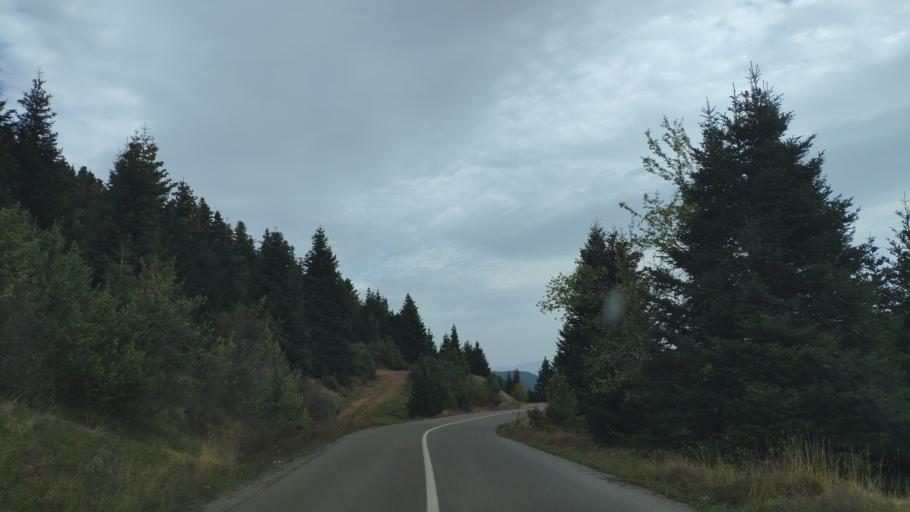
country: GR
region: Central Greece
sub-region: Nomos Fokidos
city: Amfissa
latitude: 38.7104
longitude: 22.3233
